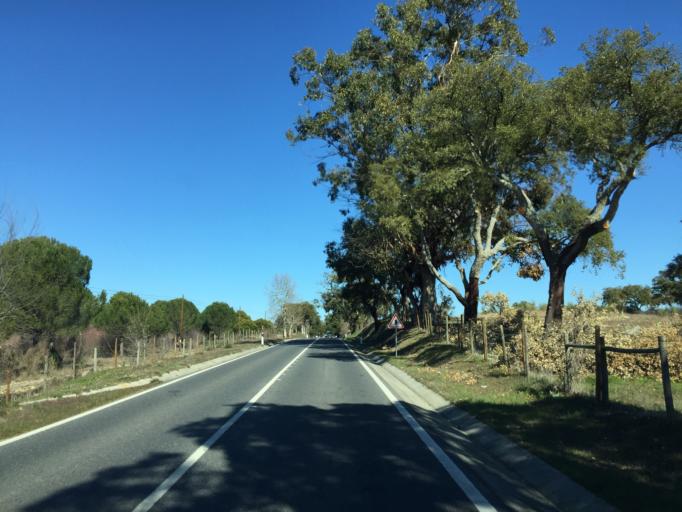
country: PT
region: Castelo Branco
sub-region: Castelo Branco
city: Castelo Branco
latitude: 39.8744
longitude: -7.4903
